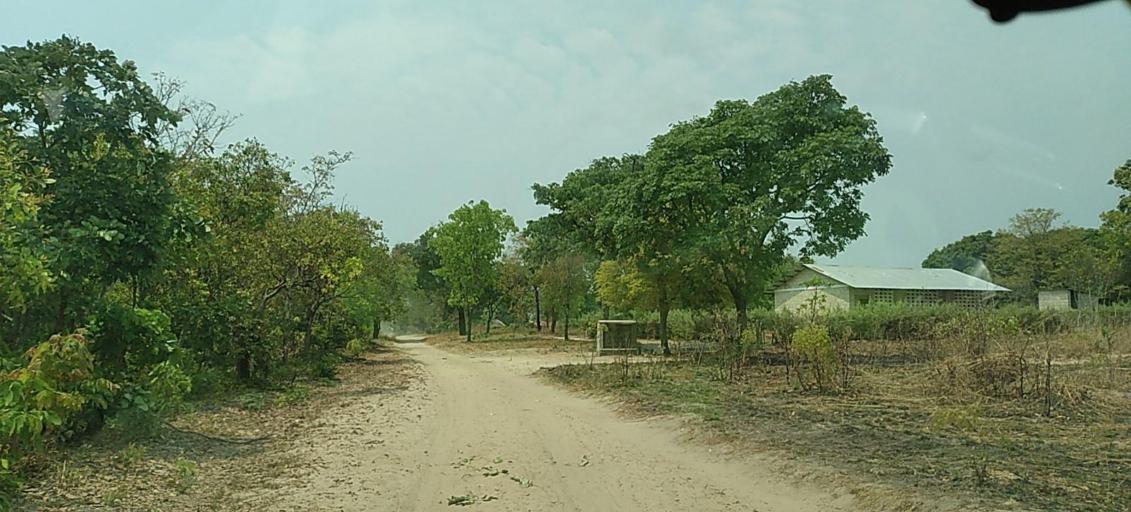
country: ZM
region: North-Western
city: Kabompo
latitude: -13.4776
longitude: 24.4572
